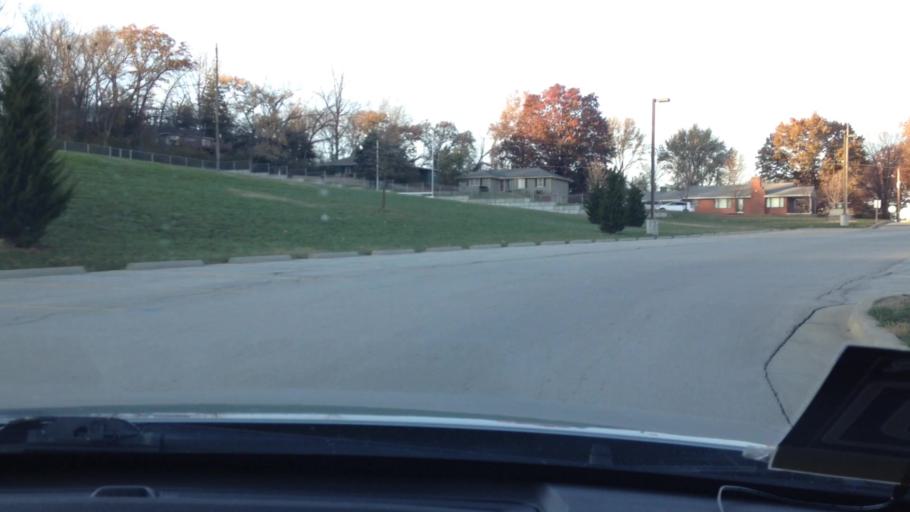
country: US
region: Kansas
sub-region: Leavenworth County
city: Leavenworth
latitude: 39.2966
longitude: -94.9311
